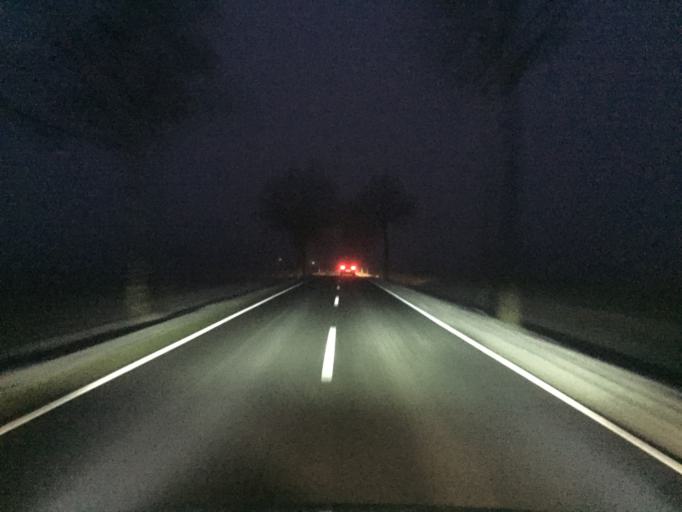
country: DE
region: Lower Saxony
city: Maasen
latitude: 52.6759
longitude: 8.8909
